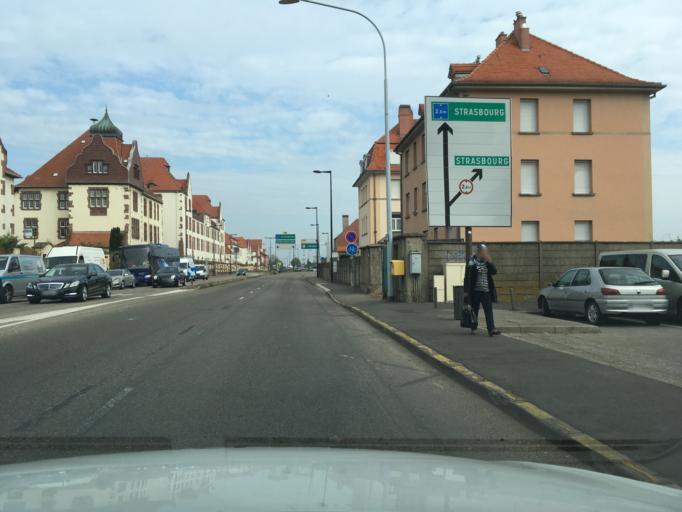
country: FR
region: Alsace
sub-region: Departement du Haut-Rhin
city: Colmar
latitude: 48.0909
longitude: 7.3603
